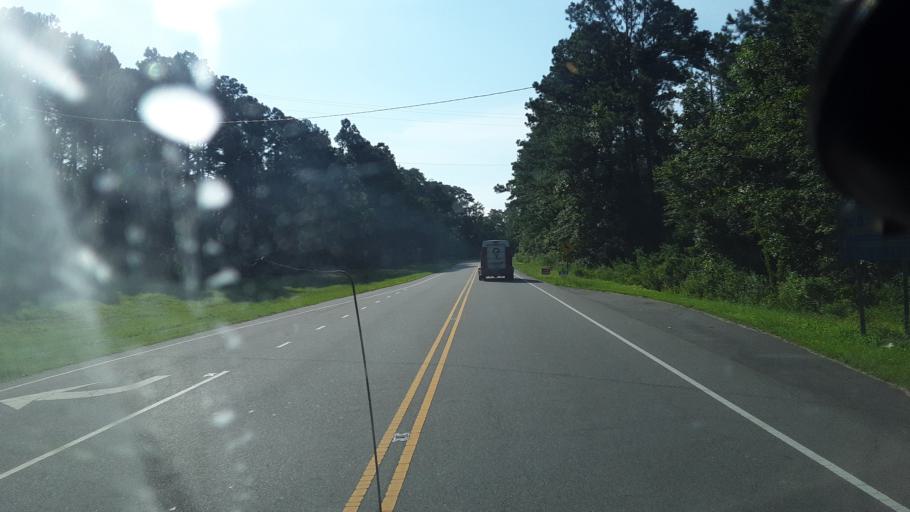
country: US
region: North Carolina
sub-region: Brunswick County
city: Belville
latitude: 34.2275
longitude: -77.9877
